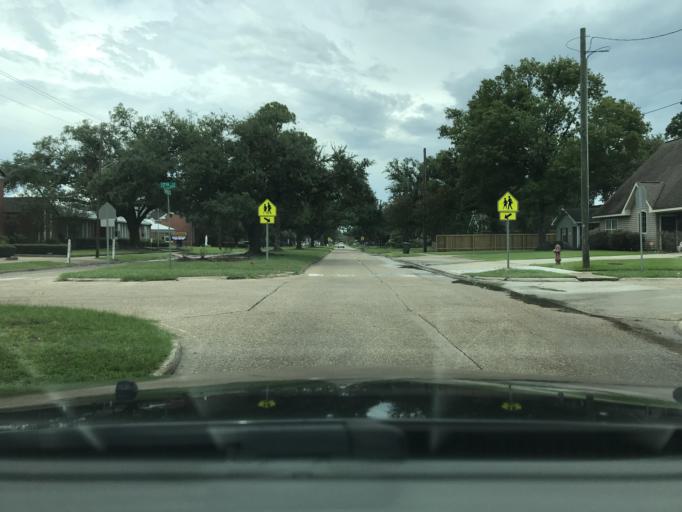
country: US
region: Louisiana
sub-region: Calcasieu Parish
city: Lake Charles
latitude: 30.2068
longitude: -93.2042
